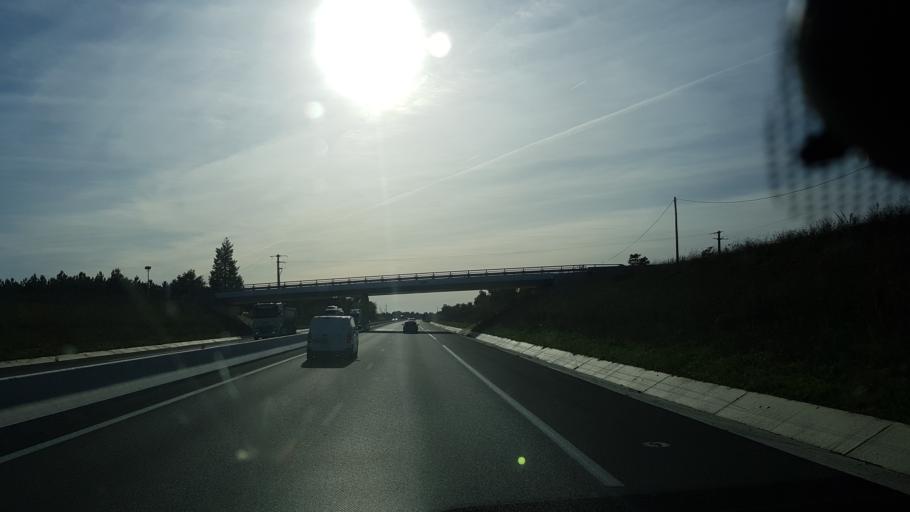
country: FR
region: Poitou-Charentes
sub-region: Departement de la Charente
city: Baignes-Sainte-Radegonde
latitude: 45.3457
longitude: -0.2075
